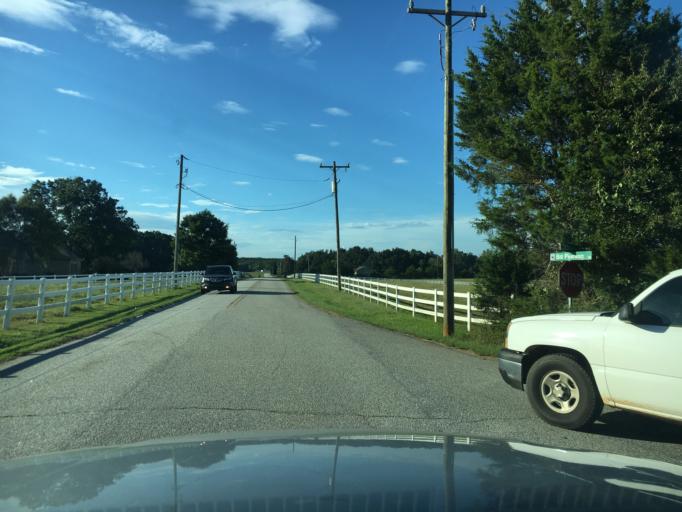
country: US
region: South Carolina
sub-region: Spartanburg County
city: Woodruff
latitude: 34.8076
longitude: -82.1026
